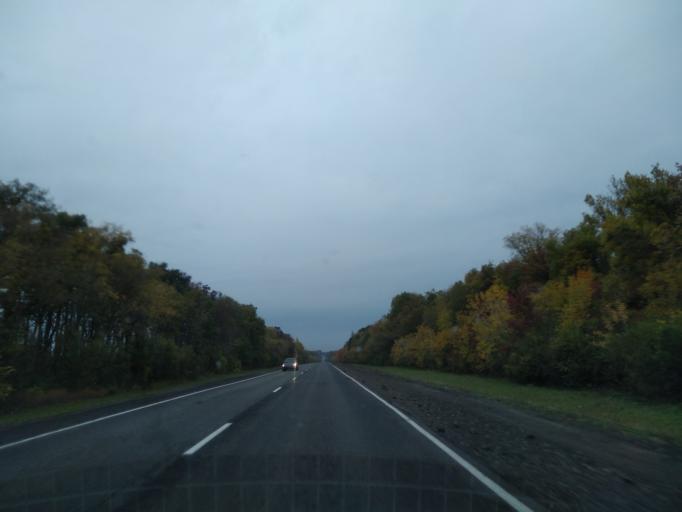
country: RU
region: Lipetsk
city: Zadonsk
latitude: 52.4701
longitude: 38.7695
